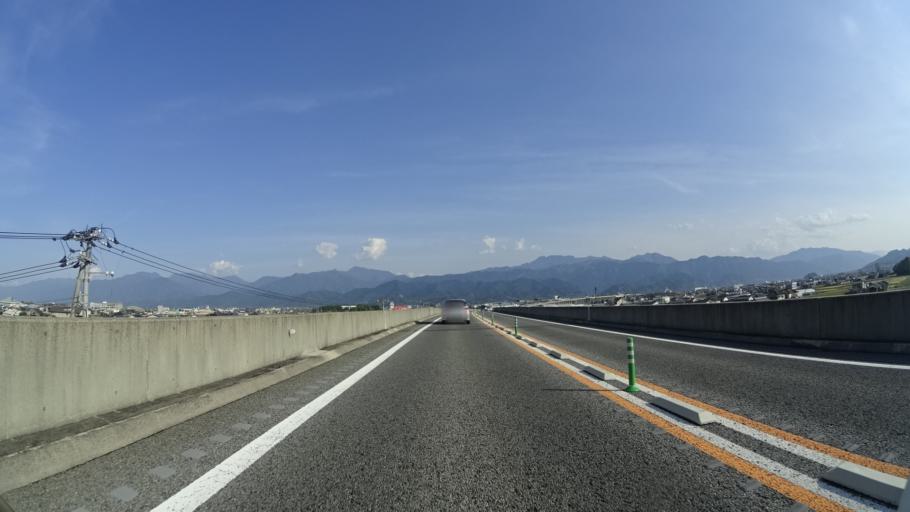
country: JP
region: Ehime
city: Saijo
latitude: 33.9291
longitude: 133.0730
